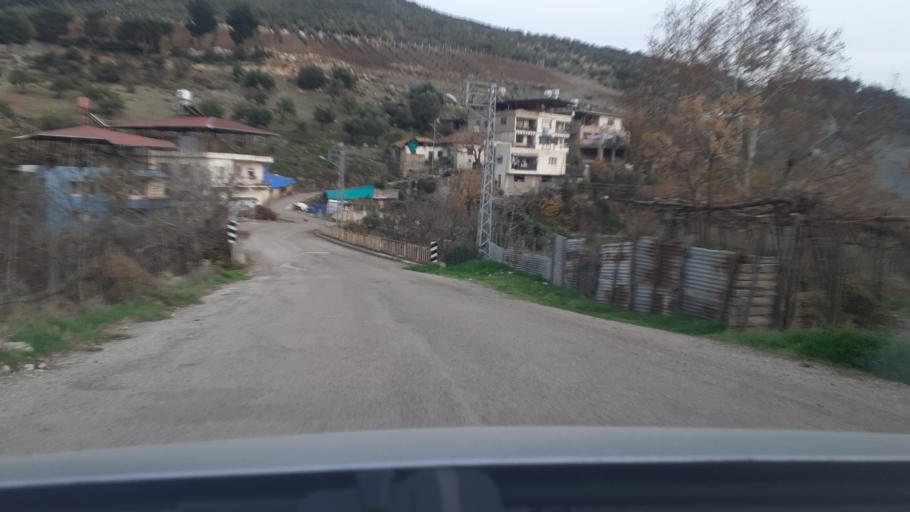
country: TR
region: Hatay
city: Kirikhan
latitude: 36.5277
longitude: 36.3168
